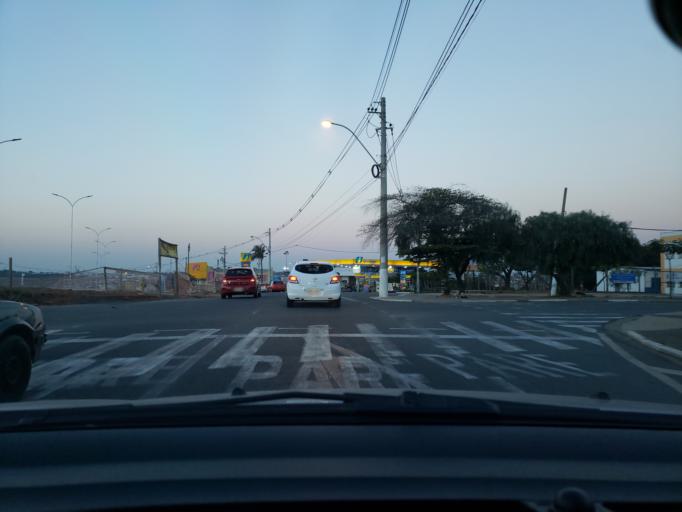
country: BR
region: Sao Paulo
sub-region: Campinas
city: Campinas
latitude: -22.9347
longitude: -47.1319
